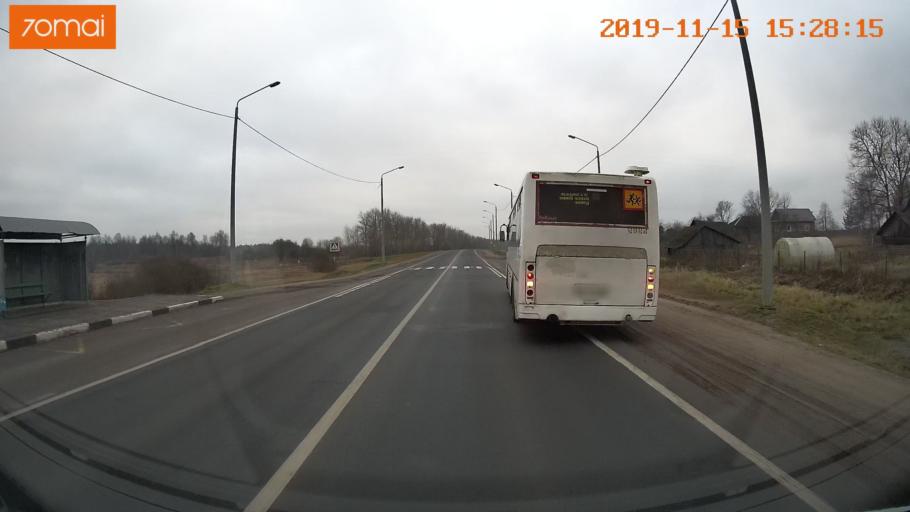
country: RU
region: Jaroslavl
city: Danilov
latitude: 58.1339
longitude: 40.1366
